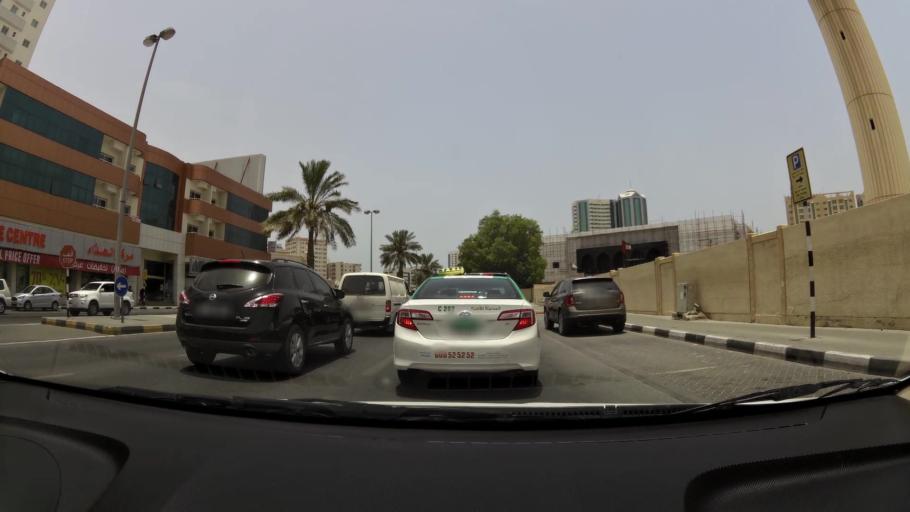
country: AE
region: Ash Shariqah
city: Sharjah
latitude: 25.3512
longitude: 55.3933
